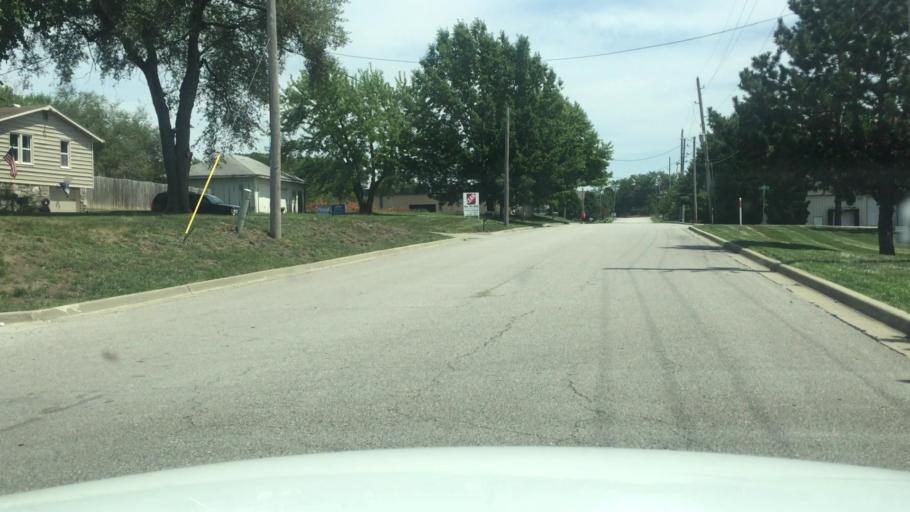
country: US
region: Missouri
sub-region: Jackson County
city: Blue Springs
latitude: 38.9871
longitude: -94.3476
